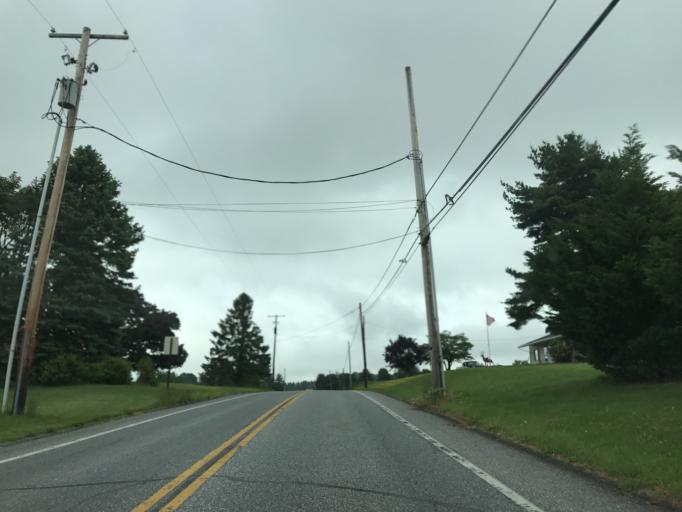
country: US
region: Pennsylvania
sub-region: York County
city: Stewartstown
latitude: 39.8232
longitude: -76.6101
